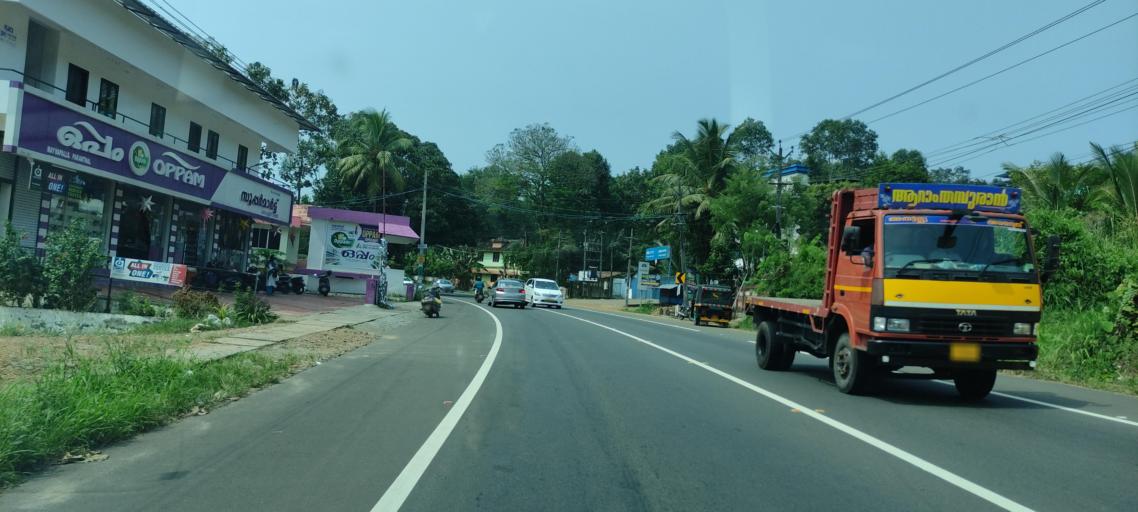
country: IN
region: Kerala
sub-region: Pattanamtitta
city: Adur
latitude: 9.1933
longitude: 76.7045
